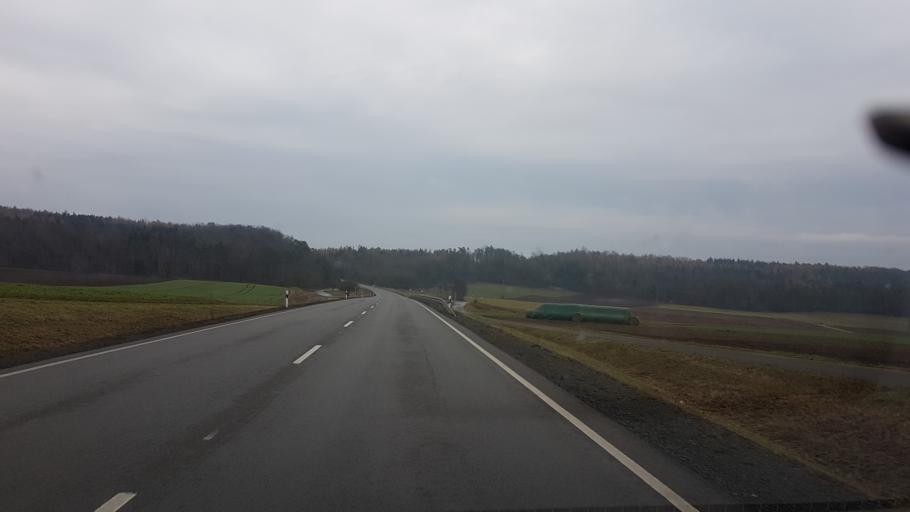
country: DE
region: Bavaria
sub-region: Regierungsbezirk Unterfranken
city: Bundorf
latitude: 50.2588
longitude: 10.5449
